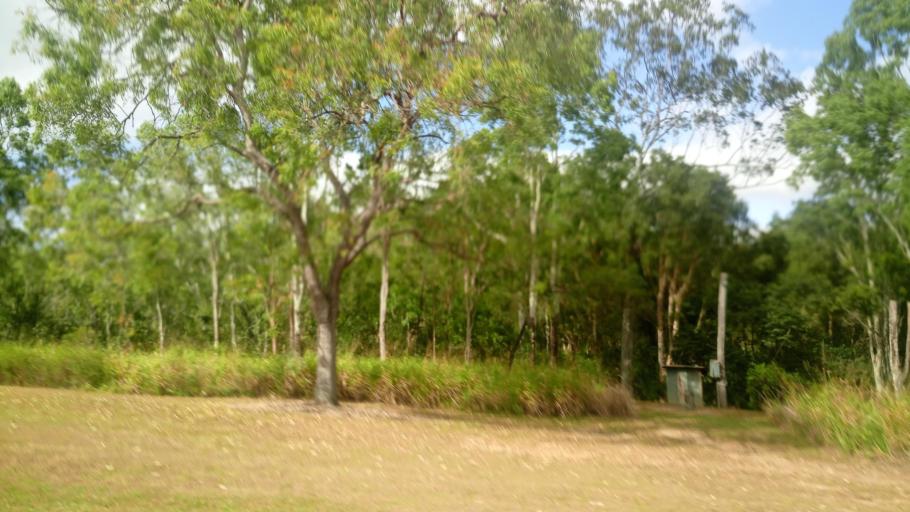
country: AU
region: Queensland
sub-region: Tablelands
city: Mareeba
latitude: -16.9757
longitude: 145.4627
